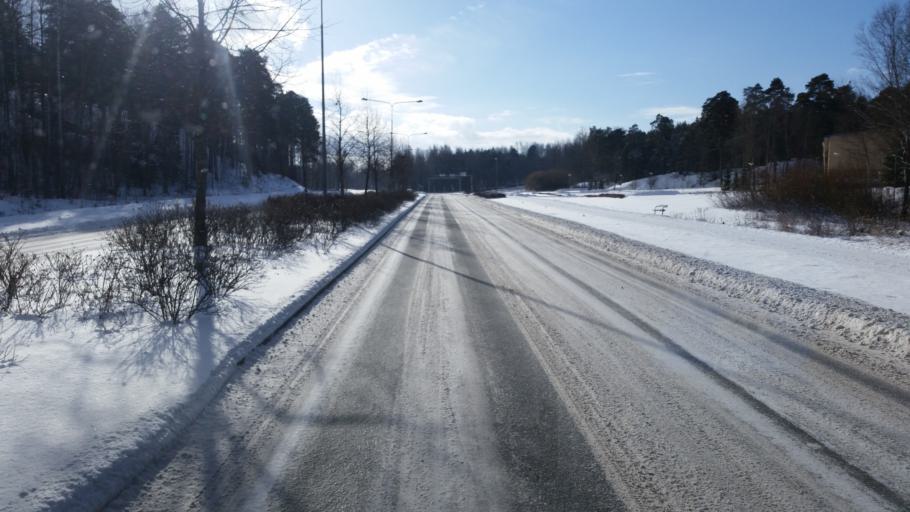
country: FI
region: Varsinais-Suomi
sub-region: Turku
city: Turku
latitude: 60.4332
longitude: 22.3178
